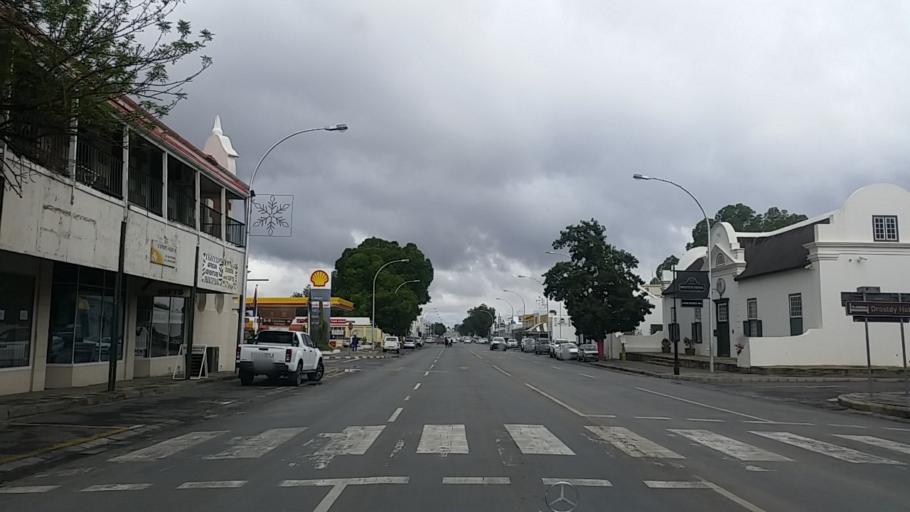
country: ZA
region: Eastern Cape
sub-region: Cacadu District Municipality
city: Graaff-Reinet
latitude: -32.2516
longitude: 24.5358
